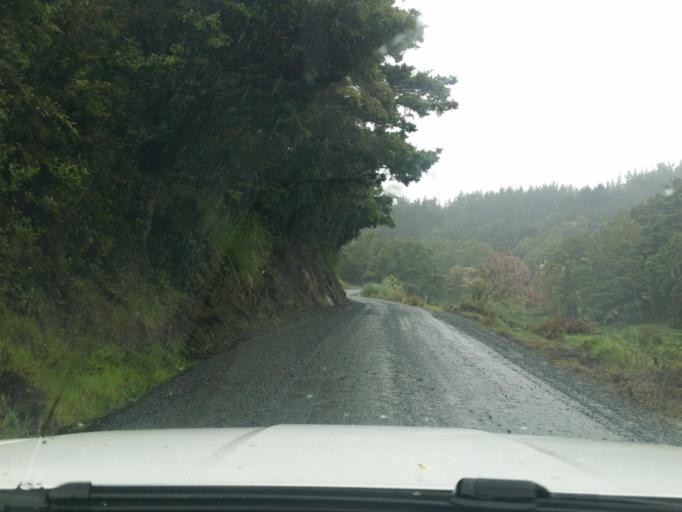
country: NZ
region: Northland
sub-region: Kaipara District
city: Dargaville
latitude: -35.8005
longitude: 173.9918
